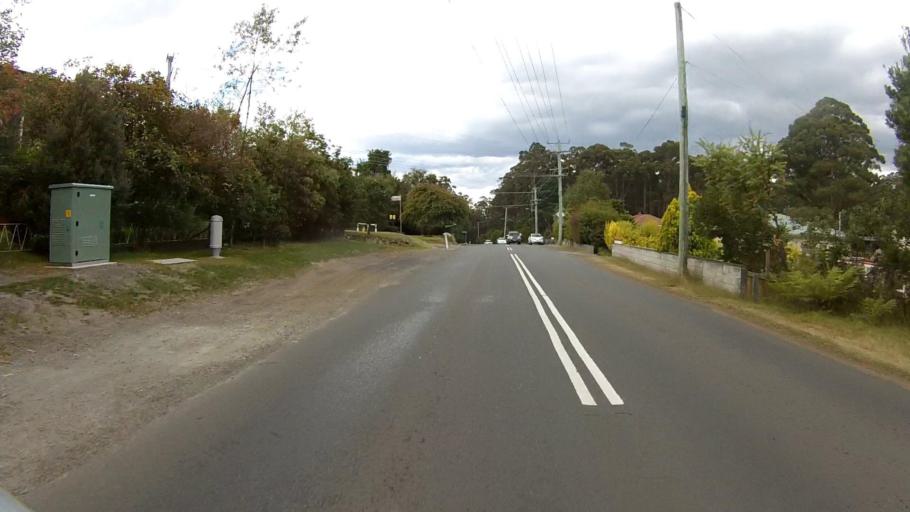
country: AU
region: Tasmania
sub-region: Hobart
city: Dynnyrne
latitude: -42.9138
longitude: 147.2683
